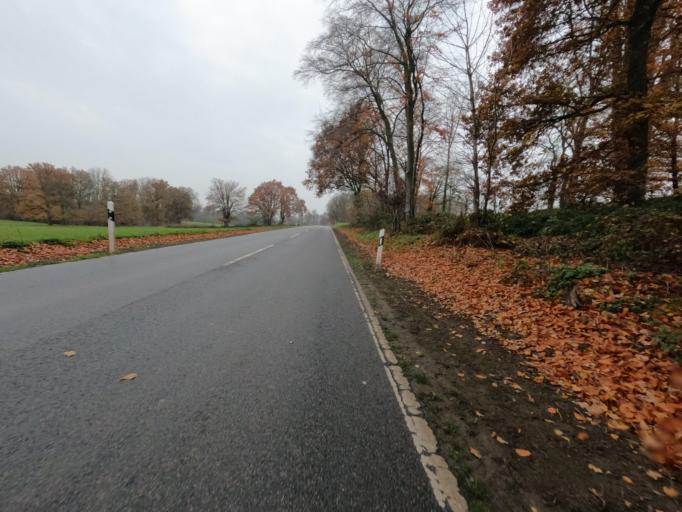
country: DE
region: North Rhine-Westphalia
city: Geilenkirchen
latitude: 50.9916
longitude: 6.1567
